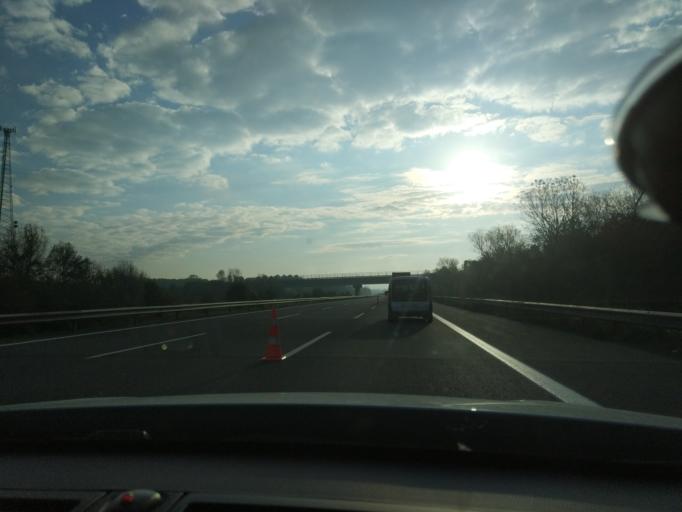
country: TR
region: Duzce
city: Duzce
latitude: 40.8117
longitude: 31.1142
